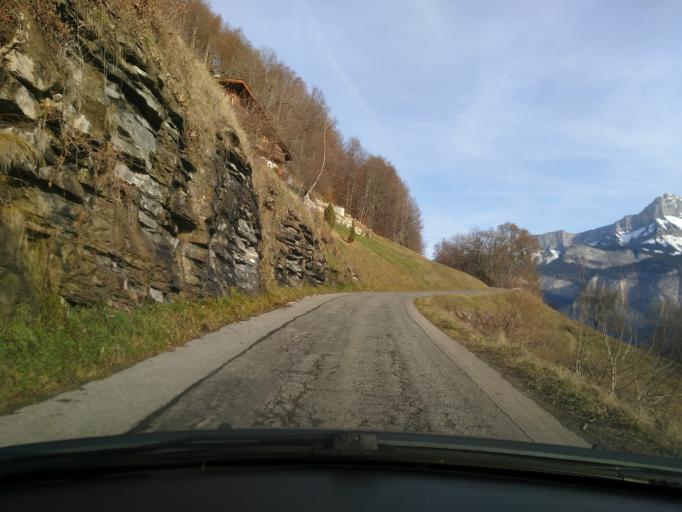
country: FR
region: Rhone-Alpes
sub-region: Departement de la Haute-Savoie
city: Sallanches
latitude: 45.9465
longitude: 6.6158
